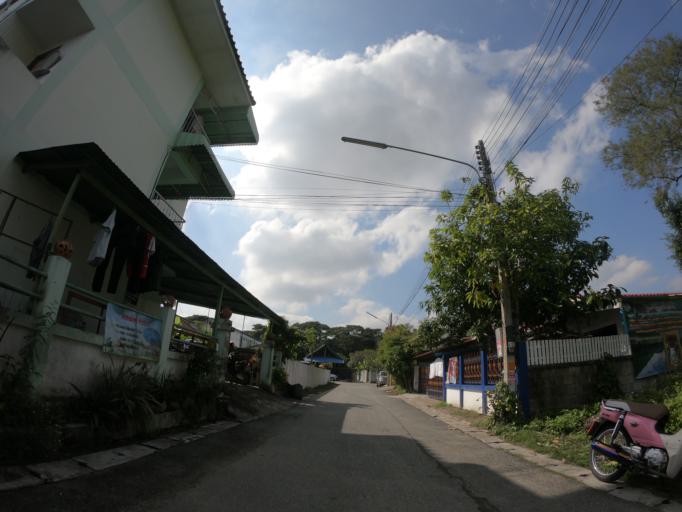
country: TH
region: Chiang Mai
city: Chiang Mai
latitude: 18.7898
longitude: 99.0328
